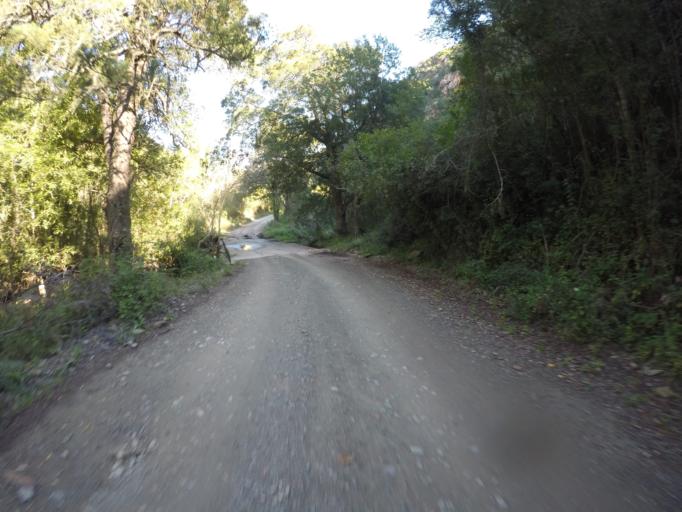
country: ZA
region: Eastern Cape
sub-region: Cacadu District Municipality
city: Kareedouw
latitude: -33.6535
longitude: 24.5205
